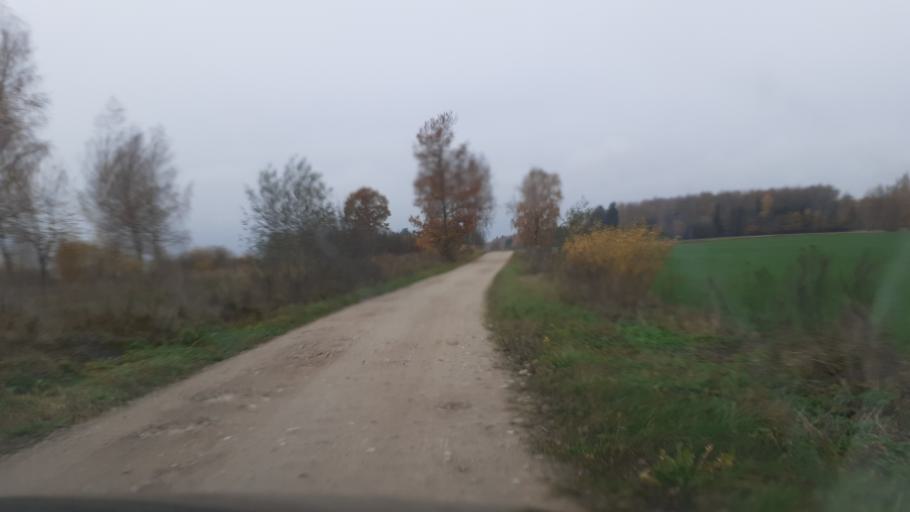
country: LV
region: Saldus Rajons
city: Saldus
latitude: 56.8703
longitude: 22.3337
